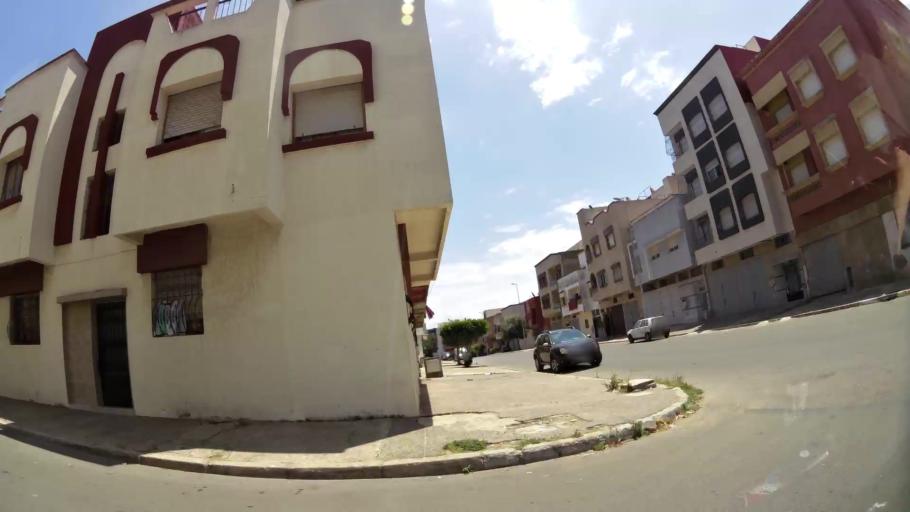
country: MA
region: Gharb-Chrarda-Beni Hssen
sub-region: Kenitra Province
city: Kenitra
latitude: 34.2683
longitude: -6.6137
